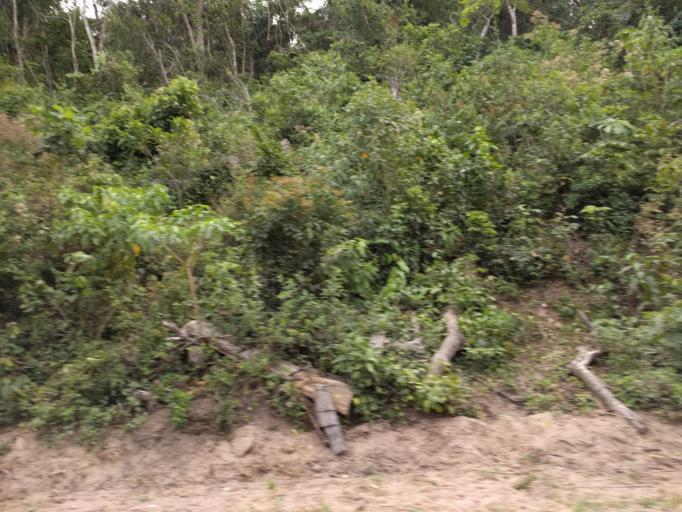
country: BO
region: Santa Cruz
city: Santiago del Torno
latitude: -17.9028
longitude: -63.4374
